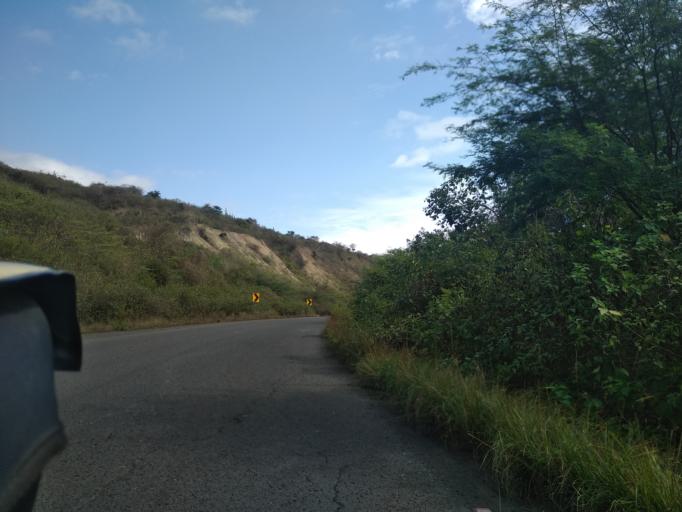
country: EC
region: Manabi
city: Jipijapa
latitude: -1.4344
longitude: -80.7535
